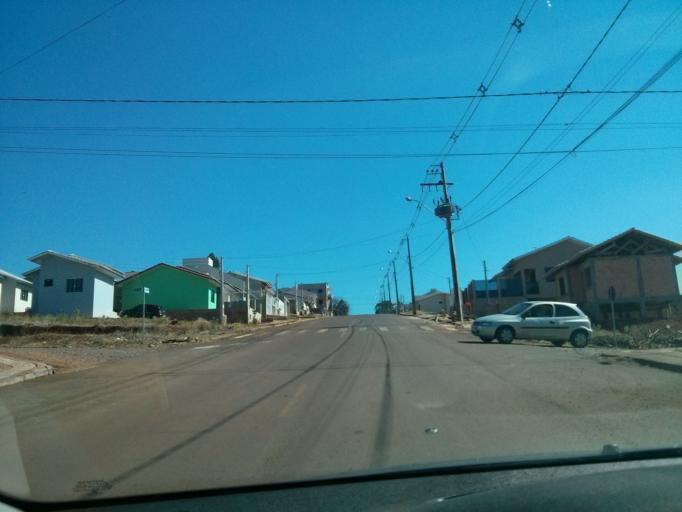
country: BR
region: Santa Catarina
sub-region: Chapeco
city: Chapeco
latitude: -27.0901
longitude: -52.6847
